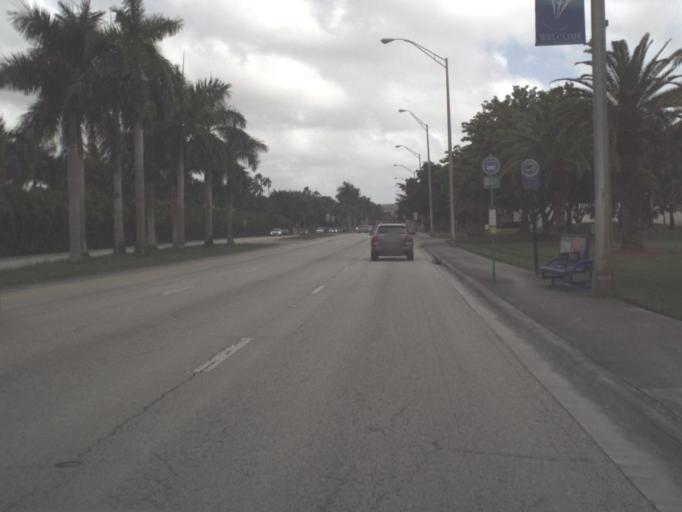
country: US
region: Florida
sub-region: Miami-Dade County
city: Doral
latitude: 25.8110
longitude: -80.3449
